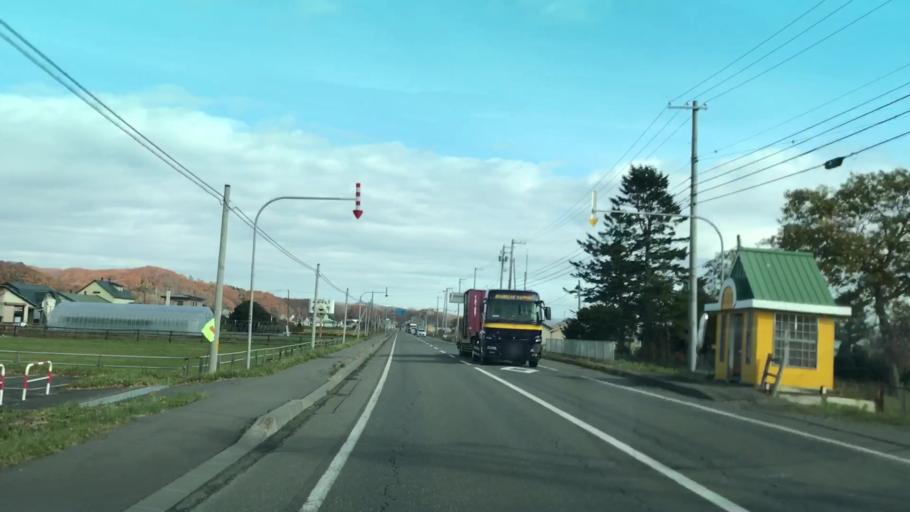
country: JP
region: Hokkaido
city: Shizunai-furukawacho
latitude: 42.5507
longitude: 142.0713
